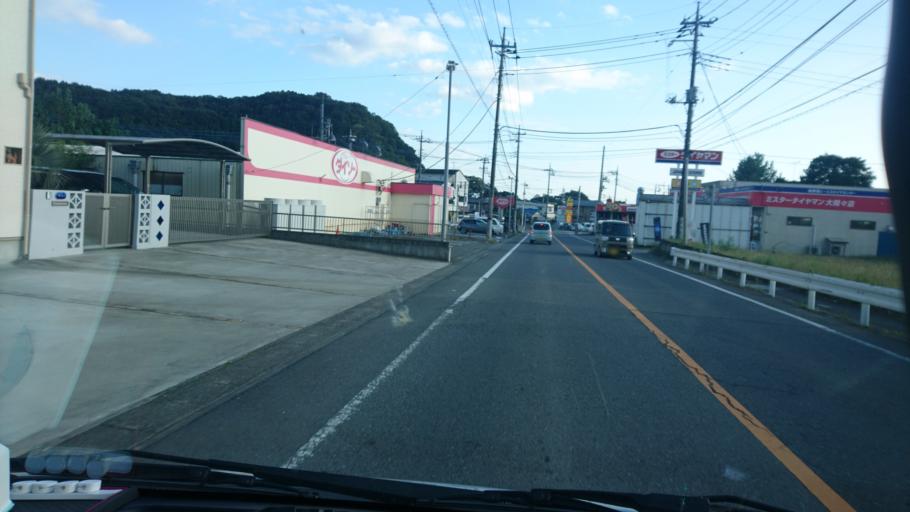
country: JP
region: Gunma
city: Omamacho-omama
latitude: 36.4420
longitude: 139.2771
